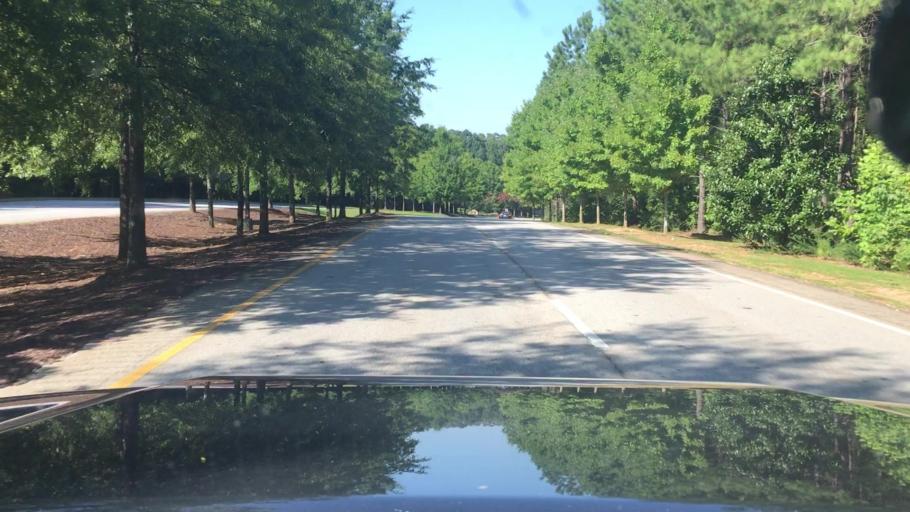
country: US
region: Georgia
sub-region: Coweta County
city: East Newnan
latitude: 33.3890
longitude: -84.7455
